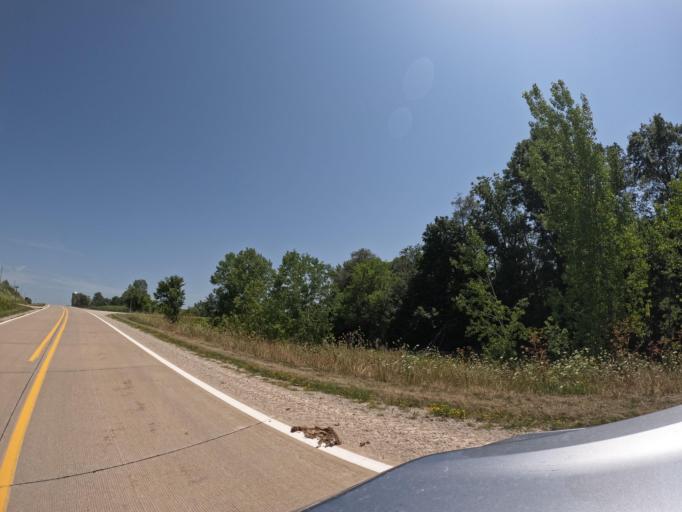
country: US
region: Iowa
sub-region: Henry County
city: Mount Pleasant
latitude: 40.9878
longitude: -91.6514
